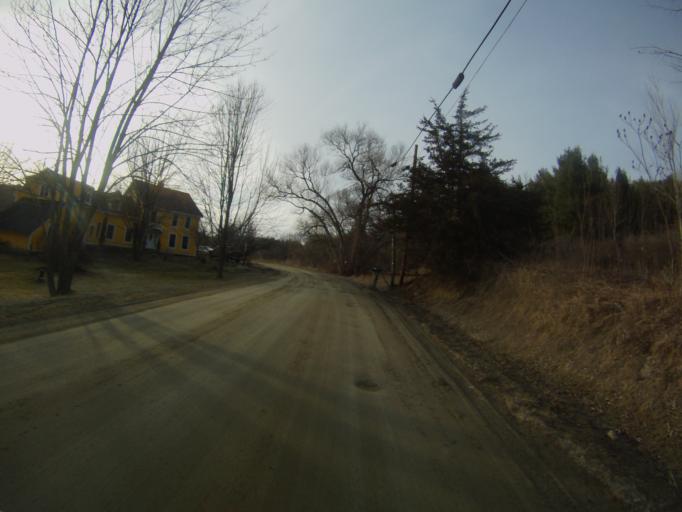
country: US
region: Vermont
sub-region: Addison County
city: Middlebury (village)
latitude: 44.0335
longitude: -73.2687
